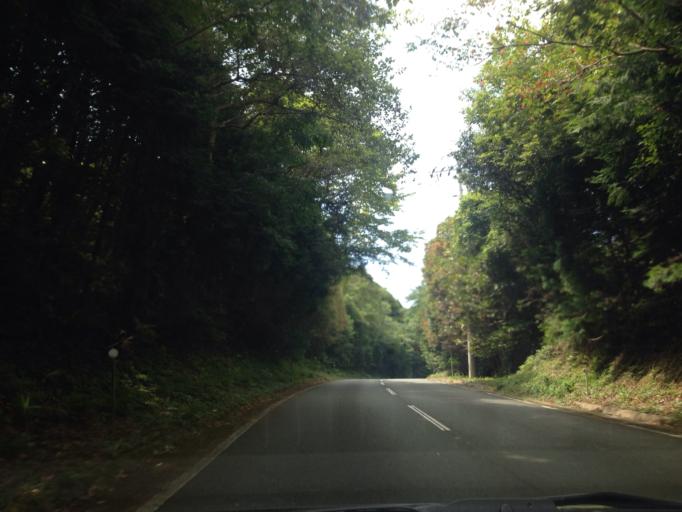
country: JP
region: Shizuoka
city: Shimoda
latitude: 34.6864
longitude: 138.7754
